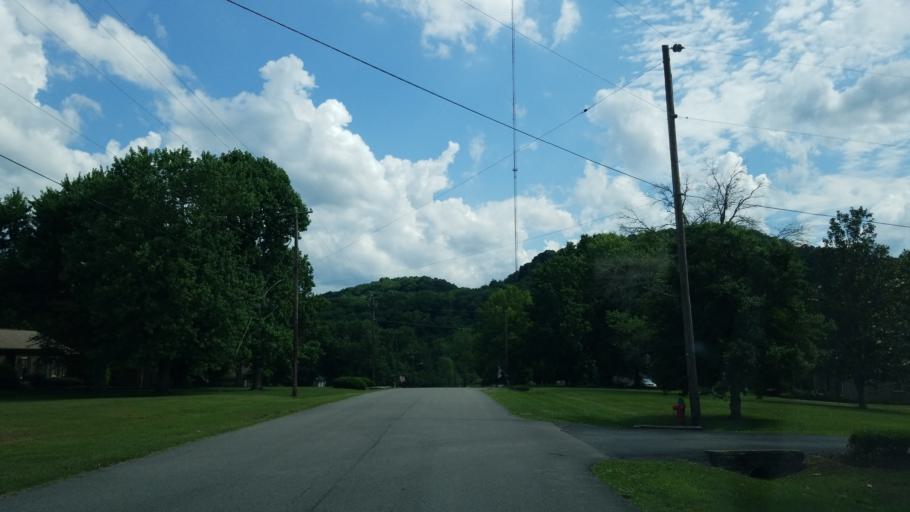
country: US
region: Tennessee
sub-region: Davidson County
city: Forest Hills
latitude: 36.0416
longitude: -86.8469
